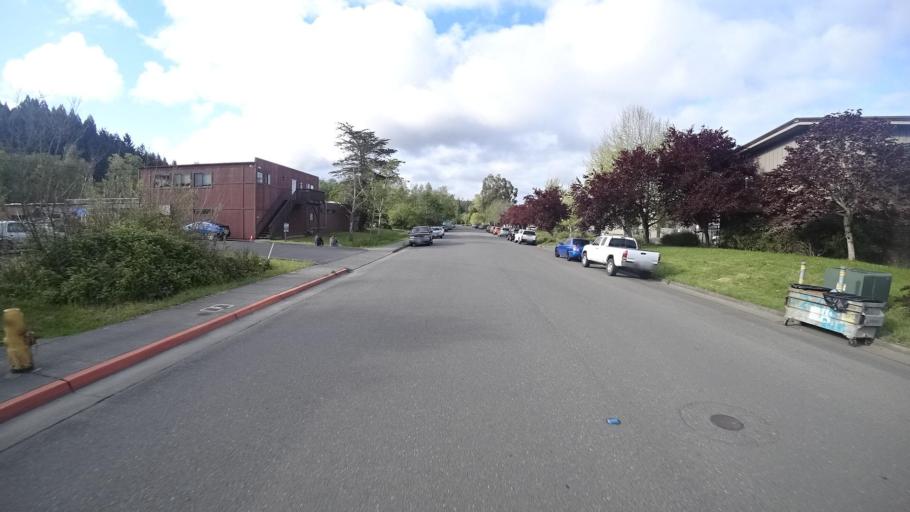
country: US
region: California
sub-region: Humboldt County
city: Arcata
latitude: 40.9042
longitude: -124.0692
